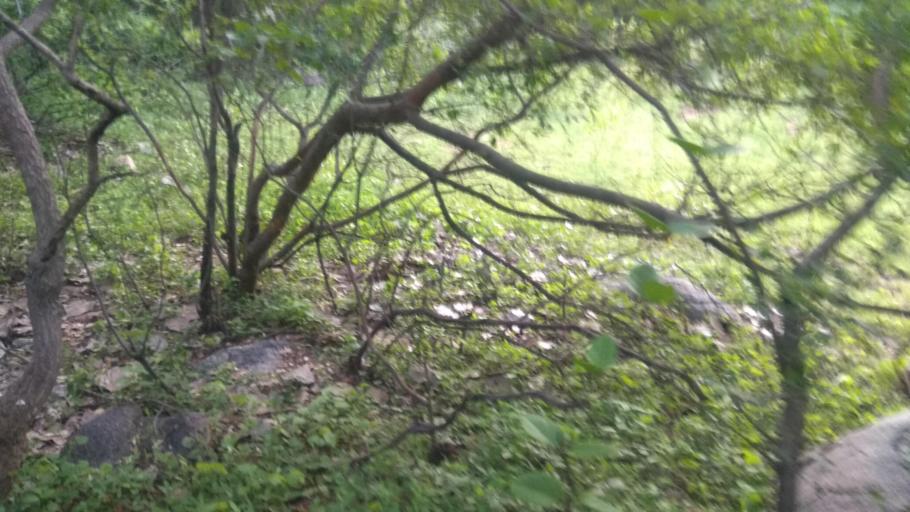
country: IN
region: Telangana
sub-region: Mahbubnagar
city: Farrukhnagar
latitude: 16.8984
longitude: 78.4910
